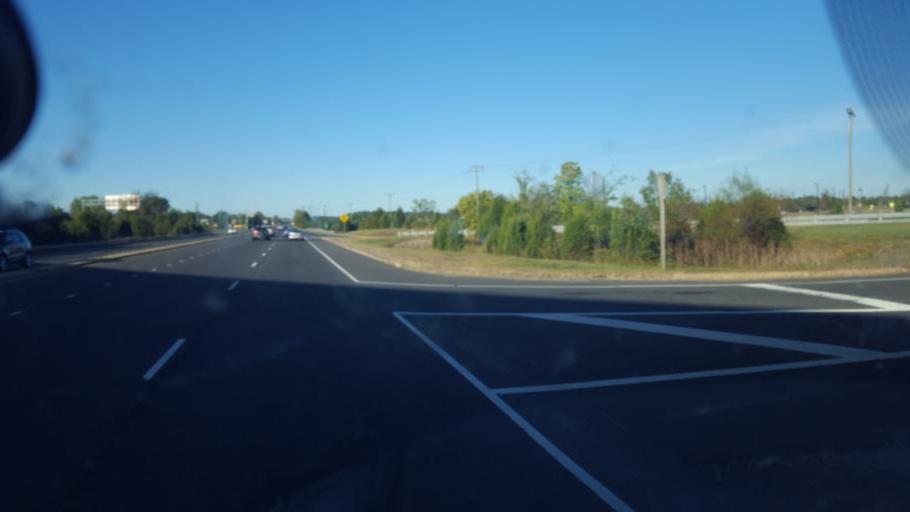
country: US
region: Virginia
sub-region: Prince William County
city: Bull Run
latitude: 38.7416
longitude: -77.5204
